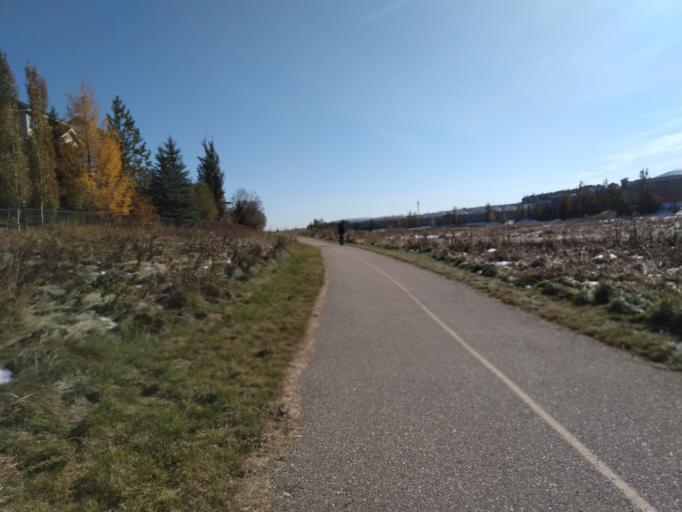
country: CA
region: Alberta
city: Calgary
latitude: 51.1650
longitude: -114.1253
